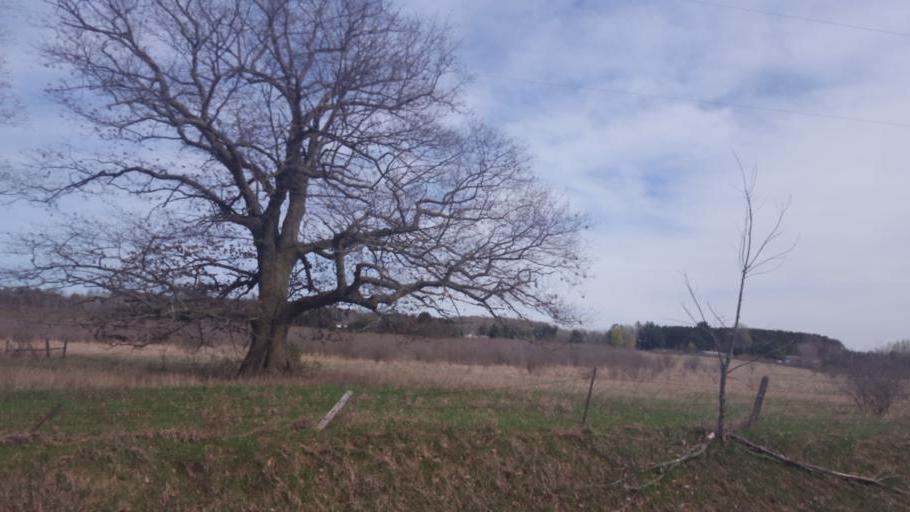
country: US
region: Michigan
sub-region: Gladwin County
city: Gladwin
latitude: 43.9826
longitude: -84.5452
